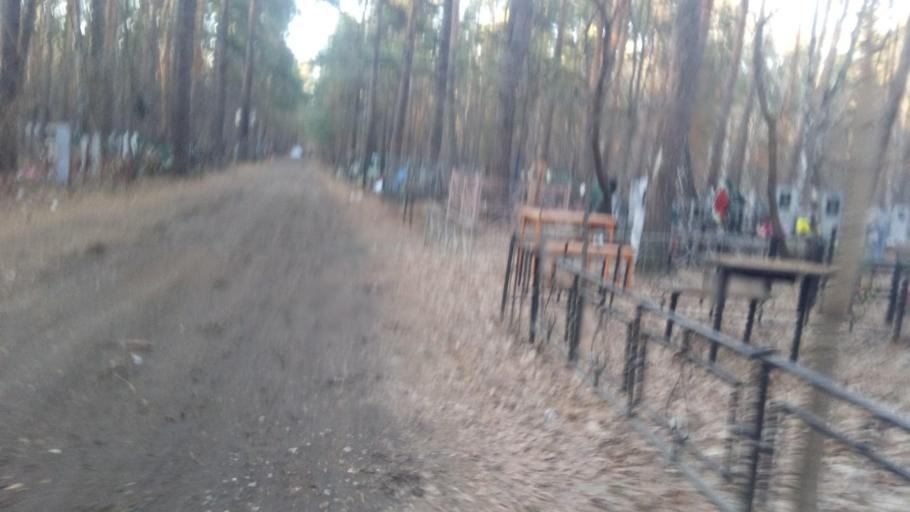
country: RU
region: Chelyabinsk
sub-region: Gorod Chelyabinsk
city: Chelyabinsk
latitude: 55.1293
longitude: 61.3493
